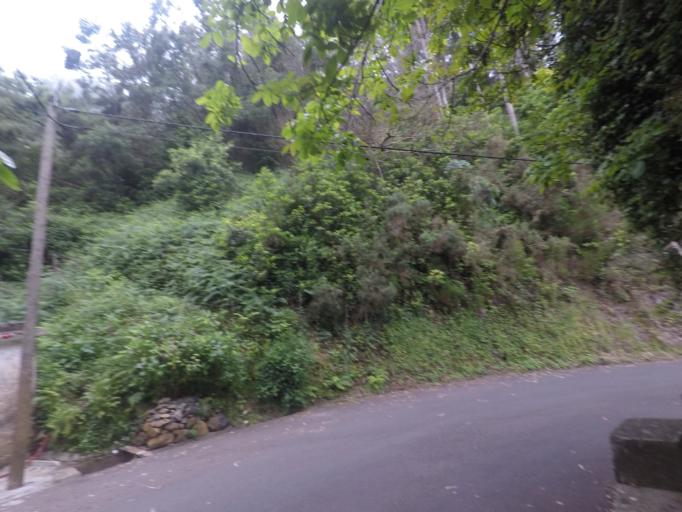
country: PT
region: Madeira
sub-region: Santana
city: Santana
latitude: 32.7438
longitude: -16.8794
